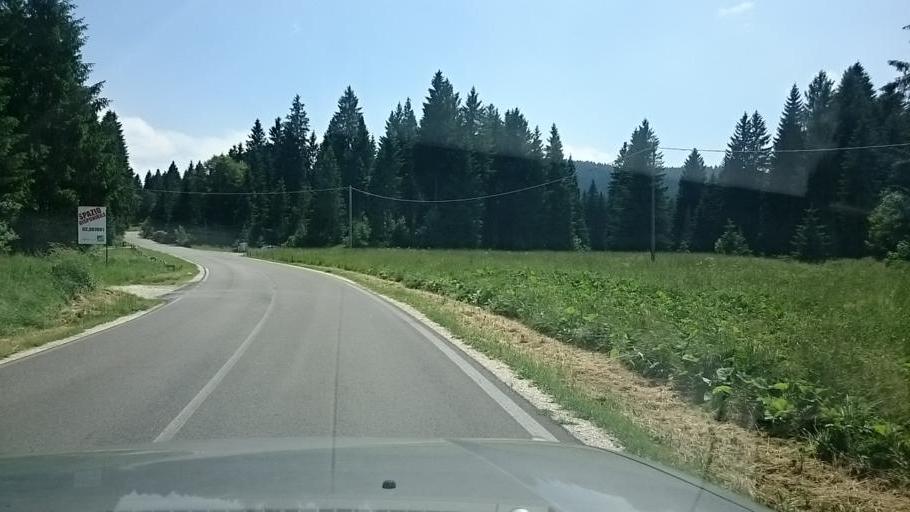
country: IT
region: Veneto
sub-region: Provincia di Vicenza
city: Gallio
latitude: 45.8543
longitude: 11.5483
